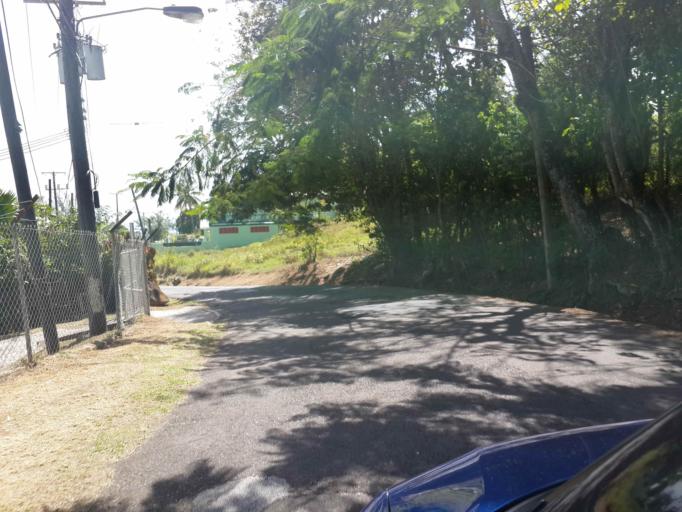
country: LC
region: Castries Quarter
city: Castries
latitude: 13.9991
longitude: -60.9988
